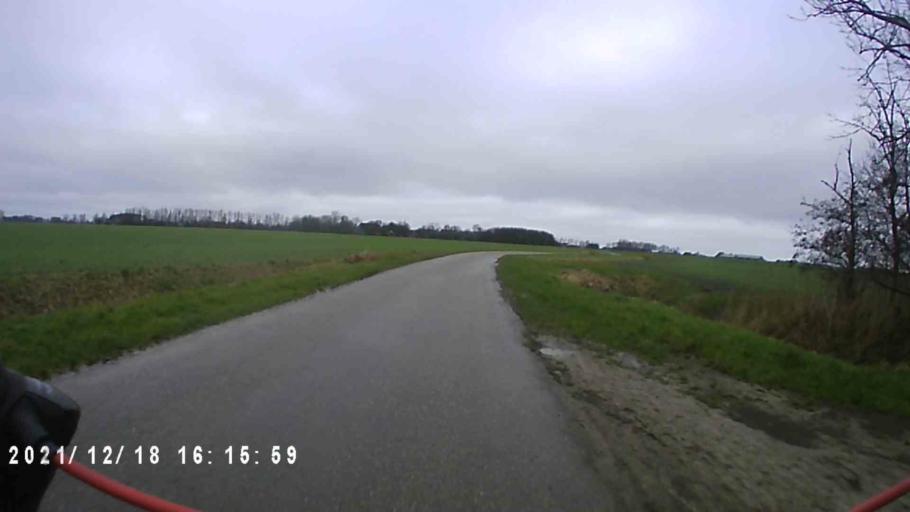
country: NL
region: Friesland
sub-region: Gemeente Dongeradeel
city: Anjum
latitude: 53.3712
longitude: 6.0603
